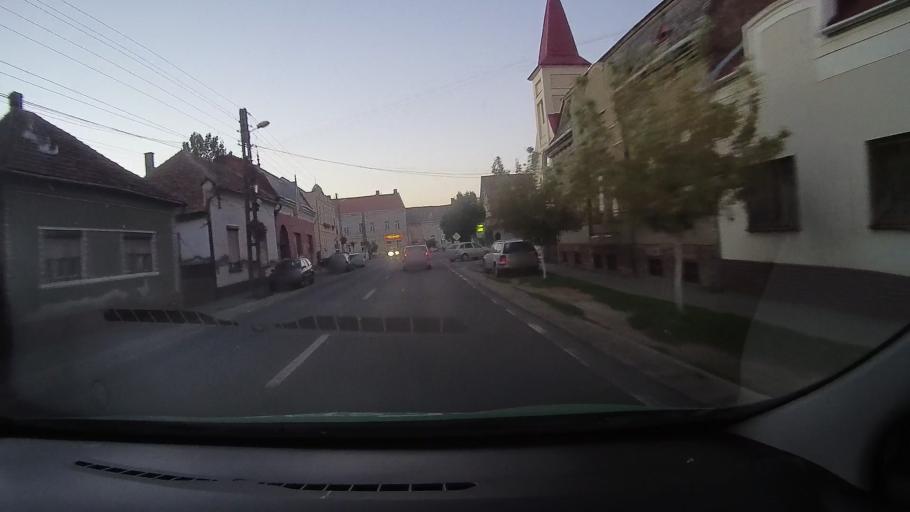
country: RO
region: Bihor
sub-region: Comuna Valea lui Mihai
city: Valea lui Mihai
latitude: 47.5158
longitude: 22.1357
